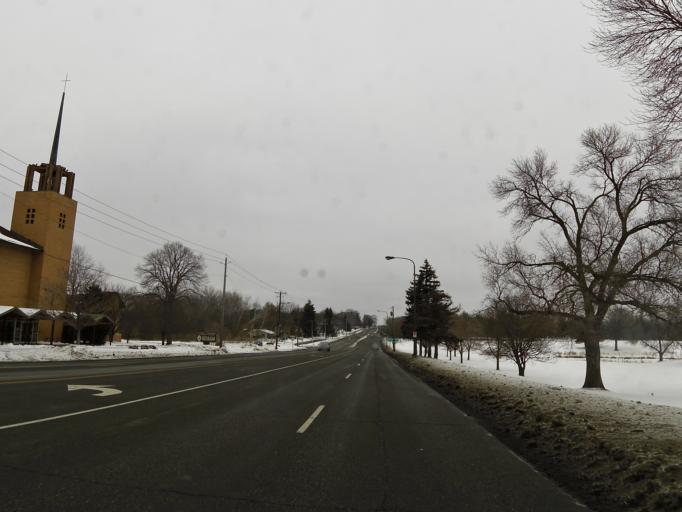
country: US
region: Minnesota
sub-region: Ramsey County
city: Little Canada
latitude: 44.9906
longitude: -93.0660
